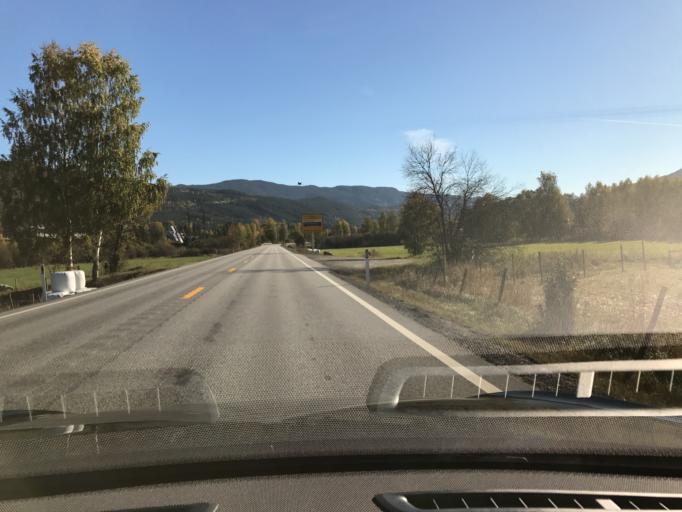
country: NO
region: Buskerud
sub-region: Nes
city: Nesbyen
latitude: 60.5763
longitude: 9.1034
